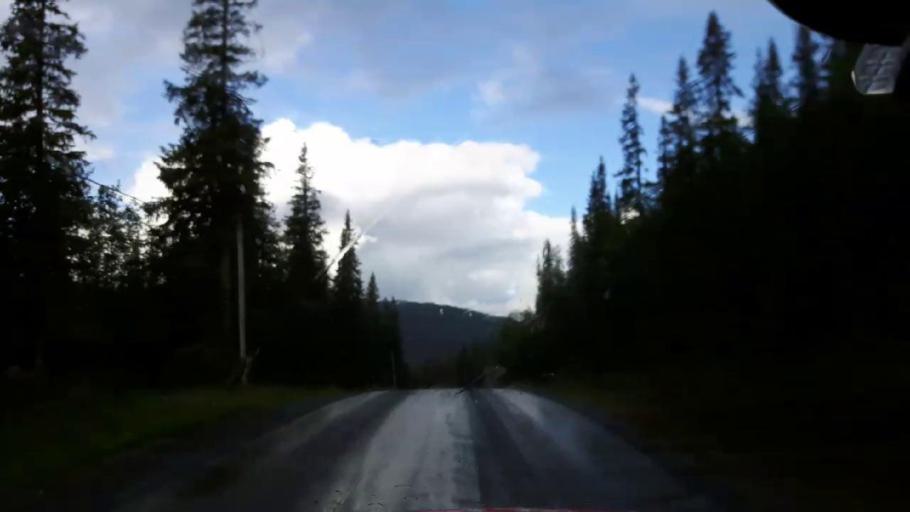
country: NO
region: Nordland
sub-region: Hattfjelldal
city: Hattfjelldal
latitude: 64.8649
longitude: 14.8944
